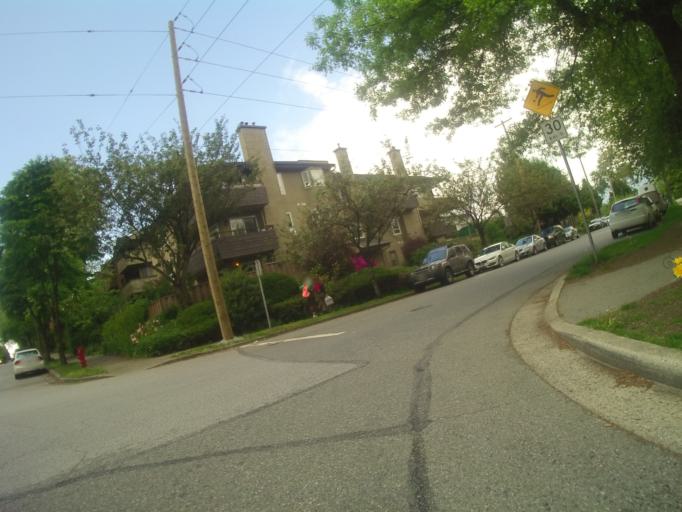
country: CA
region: British Columbia
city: Vancouver
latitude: 49.2643
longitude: -123.0851
